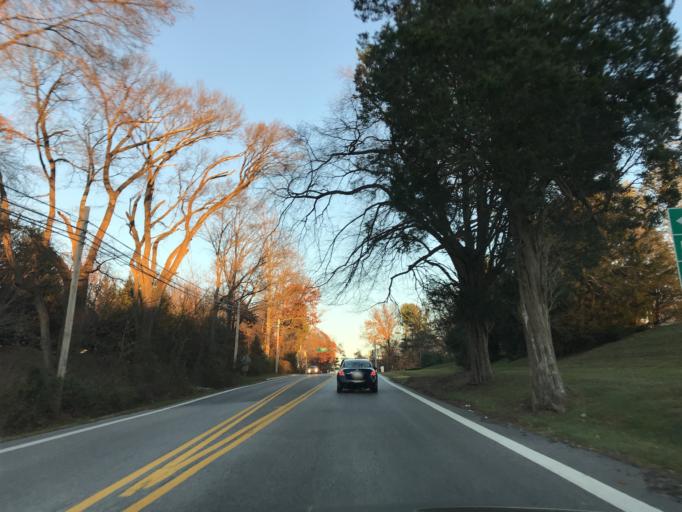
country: US
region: Maryland
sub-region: Howard County
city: Riverside
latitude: 39.2331
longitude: -76.9010
